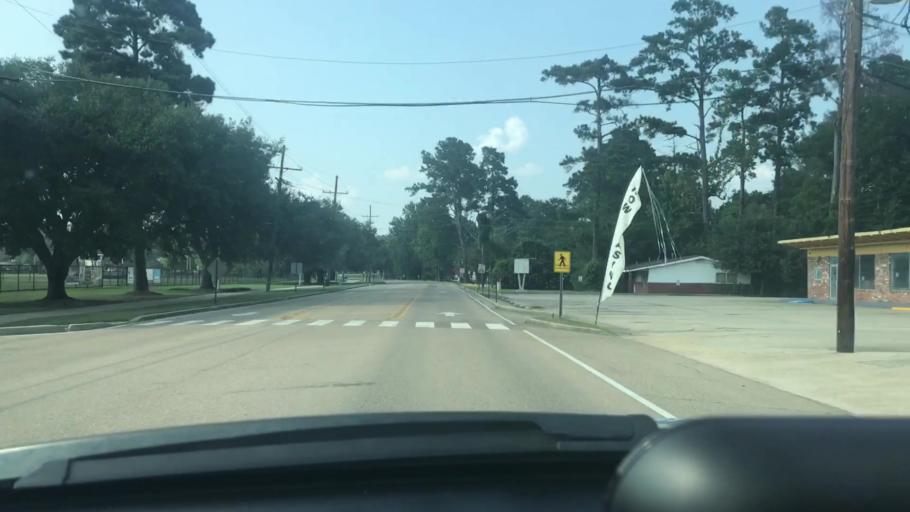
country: US
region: Louisiana
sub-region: Tangipahoa Parish
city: Hammond
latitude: 30.5159
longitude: -90.4657
